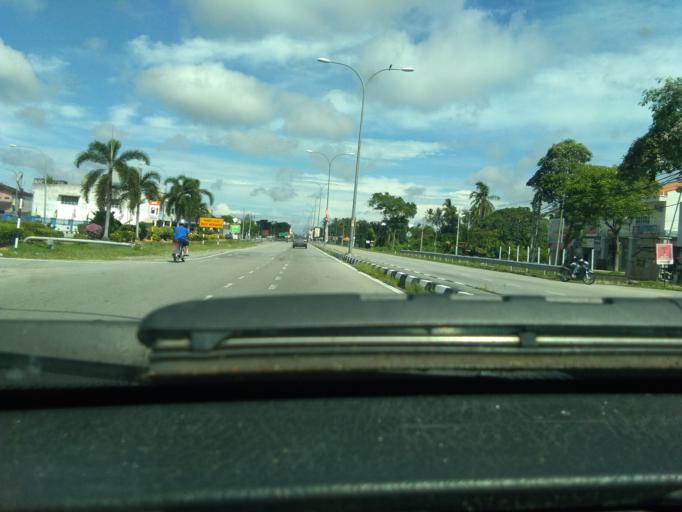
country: MY
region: Perak
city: Bagan Serai
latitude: 5.0054
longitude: 100.5445
